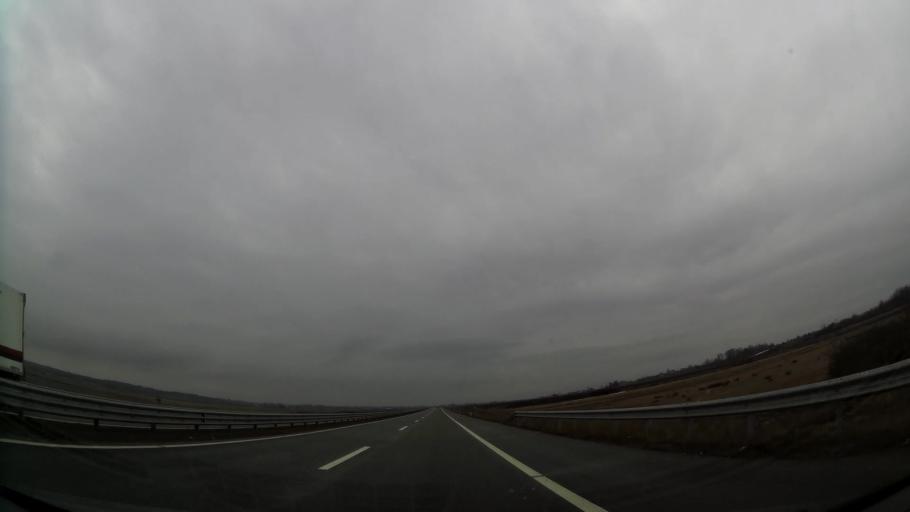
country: XK
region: Ferizaj
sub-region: Komuna e Ferizajt
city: Ferizaj
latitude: 42.4285
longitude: 21.2001
